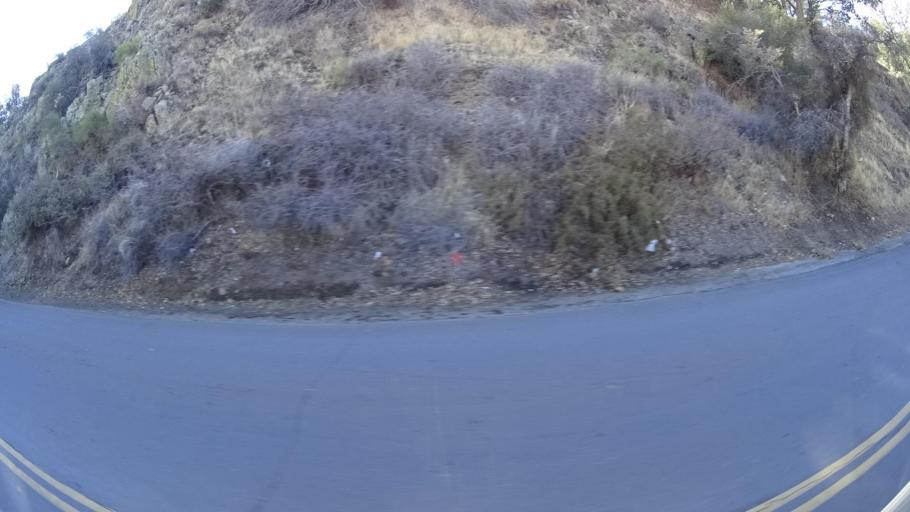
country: US
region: California
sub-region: Kern County
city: Kernville
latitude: 35.7545
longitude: -118.4266
